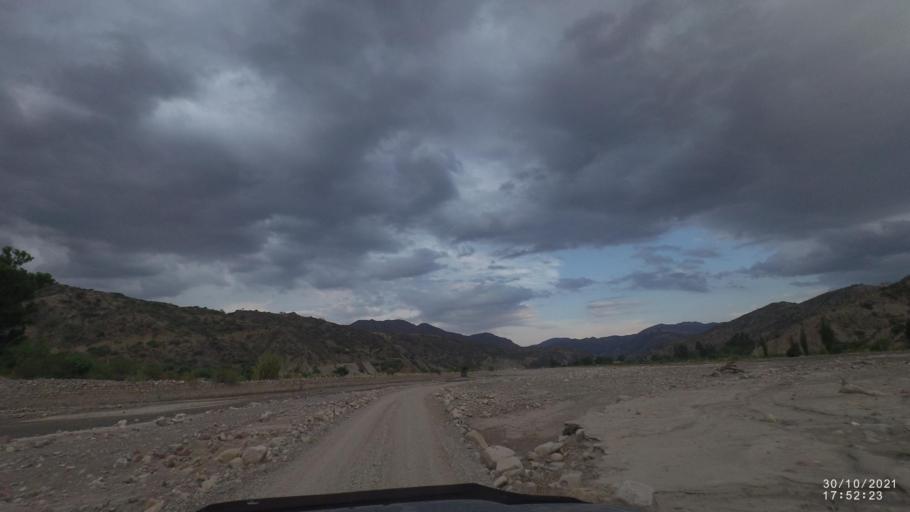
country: BO
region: Cochabamba
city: Sipe Sipe
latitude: -17.5377
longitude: -66.4994
